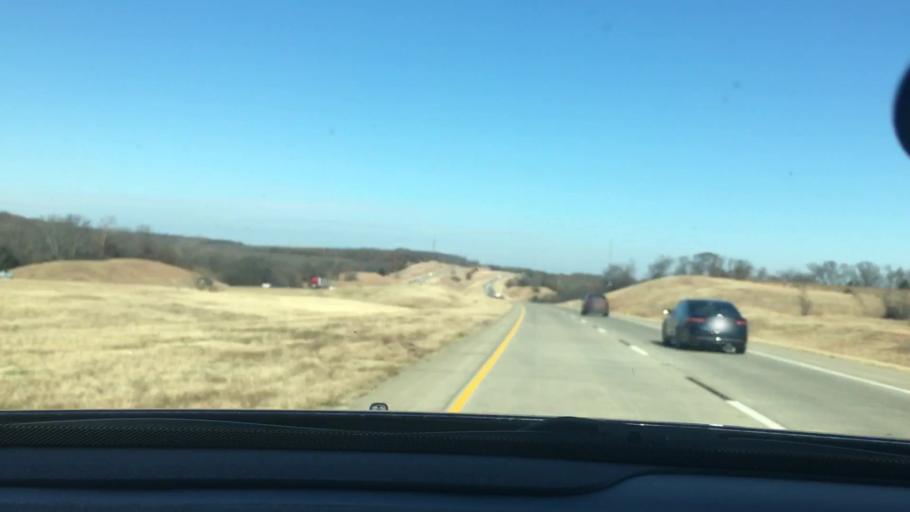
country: US
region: Oklahoma
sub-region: Love County
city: Marietta
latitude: 33.9815
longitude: -97.1352
